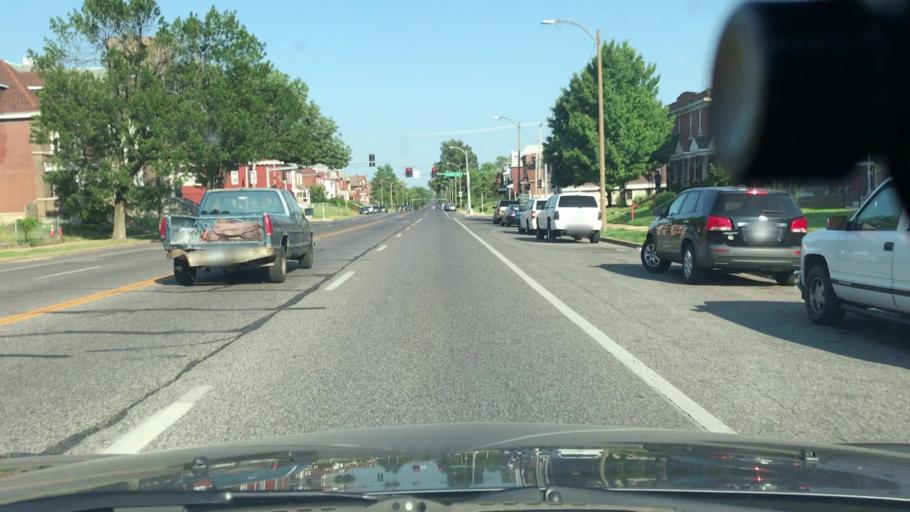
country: US
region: Missouri
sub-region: Saint Louis County
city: Hillsdale
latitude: 38.6536
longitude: -90.2450
